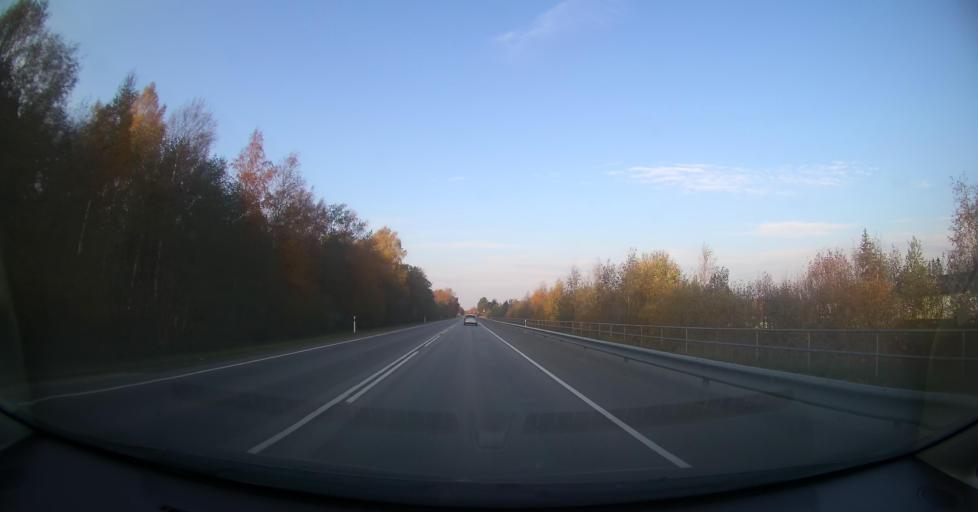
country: EE
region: Laeaene
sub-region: Ridala Parish
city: Uuemoisa
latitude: 58.9491
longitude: 23.6361
